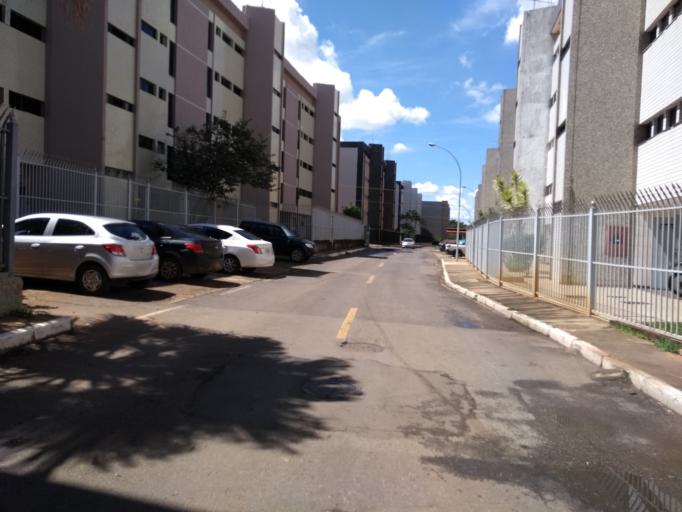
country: BR
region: Federal District
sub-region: Brasilia
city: Brasilia
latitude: -15.7955
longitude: -47.9347
